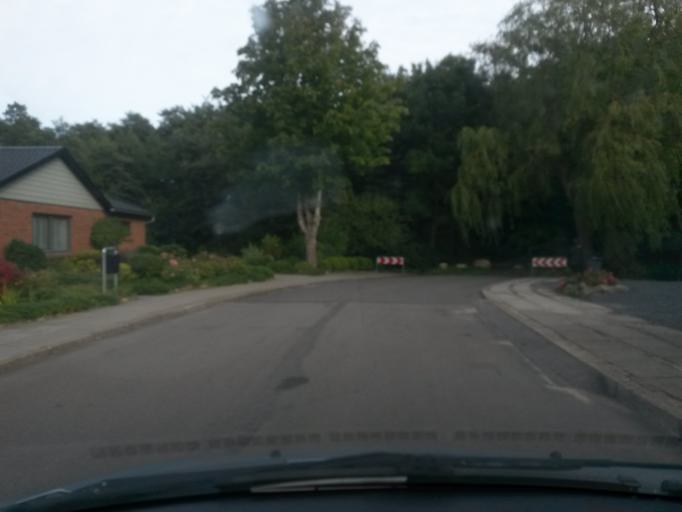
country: DK
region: Central Jutland
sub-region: Silkeborg Kommune
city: Kjellerup
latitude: 56.2888
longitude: 9.4435
